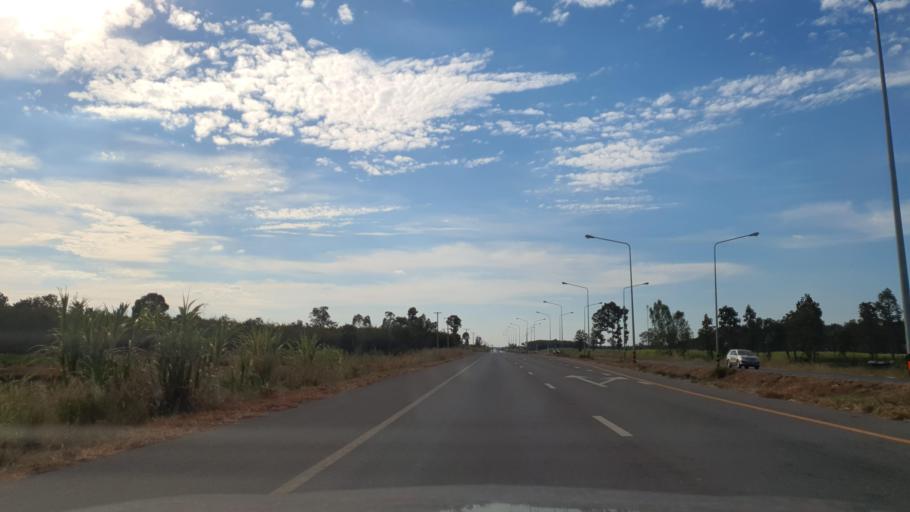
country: TH
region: Roi Et
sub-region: Amphoe Pho Chai
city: Pho Chai
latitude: 16.4153
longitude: 103.8114
